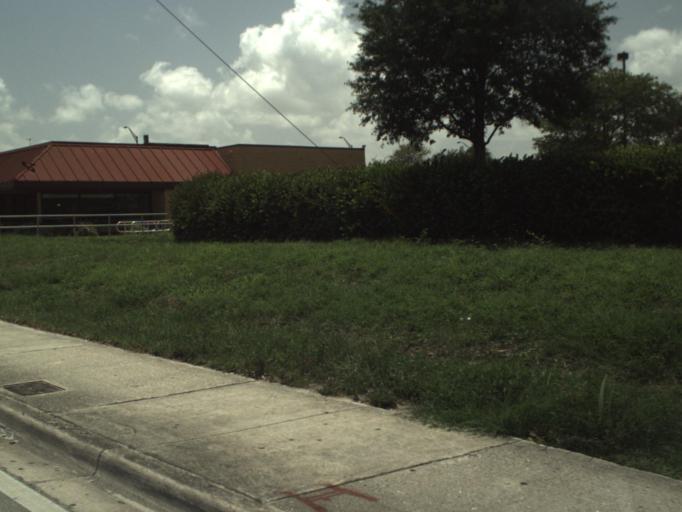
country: US
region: Florida
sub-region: Broward County
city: Twin Lakes
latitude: 26.1675
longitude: -80.1547
